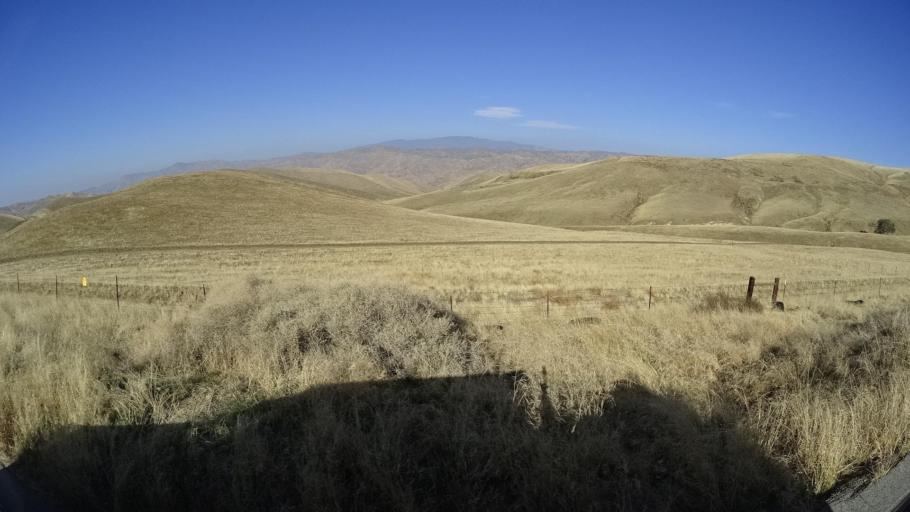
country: US
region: California
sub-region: Kern County
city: Bear Valley Springs
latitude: 35.2713
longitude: -118.6850
